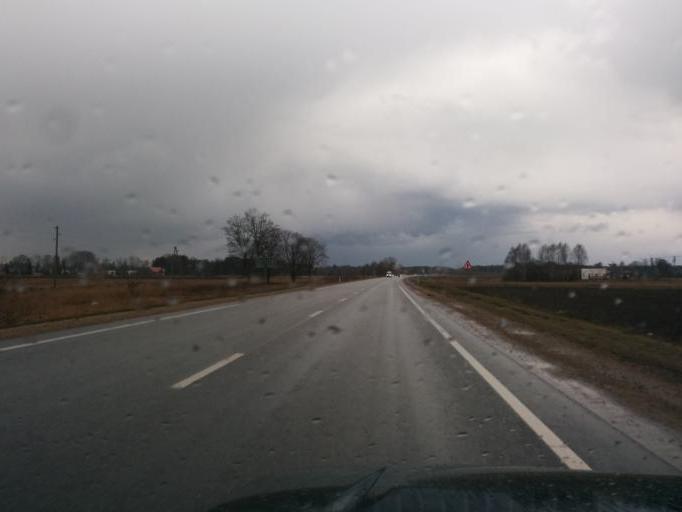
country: LV
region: Olaine
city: Olaine
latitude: 56.8701
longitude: 23.9652
